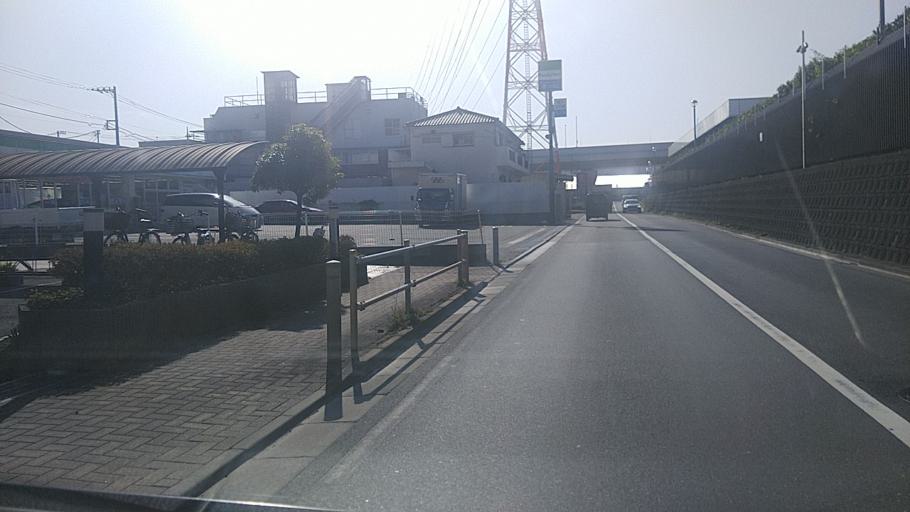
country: JP
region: Saitama
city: Wako
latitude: 35.7957
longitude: 139.6430
